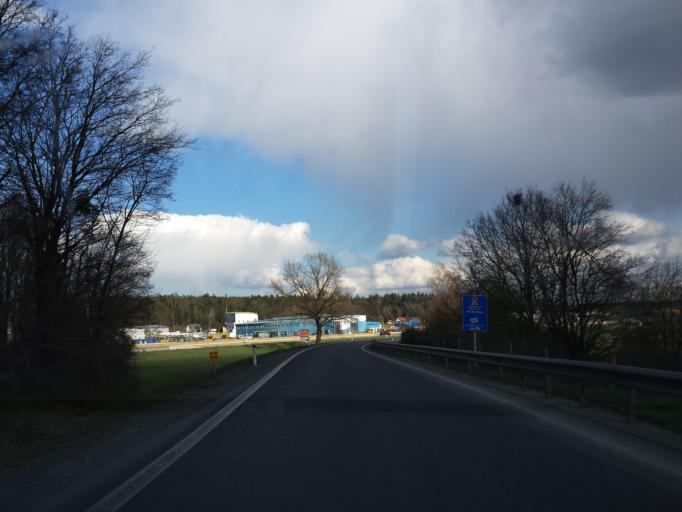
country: AT
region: Styria
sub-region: Politischer Bezirk Deutschlandsberg
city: Lannach
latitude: 46.9587
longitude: 15.3491
